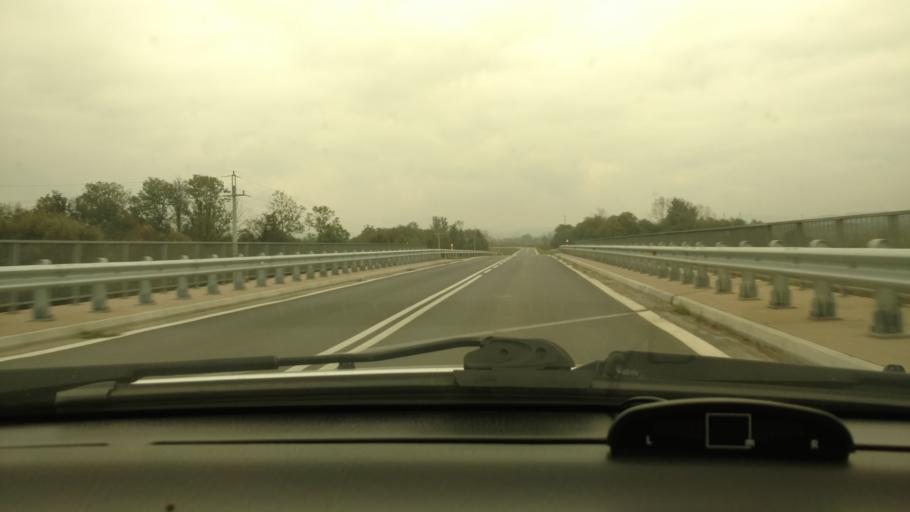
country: PL
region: Lesser Poland Voivodeship
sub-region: Powiat nowosadecki
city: Stary Sacz
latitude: 49.5908
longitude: 20.6364
